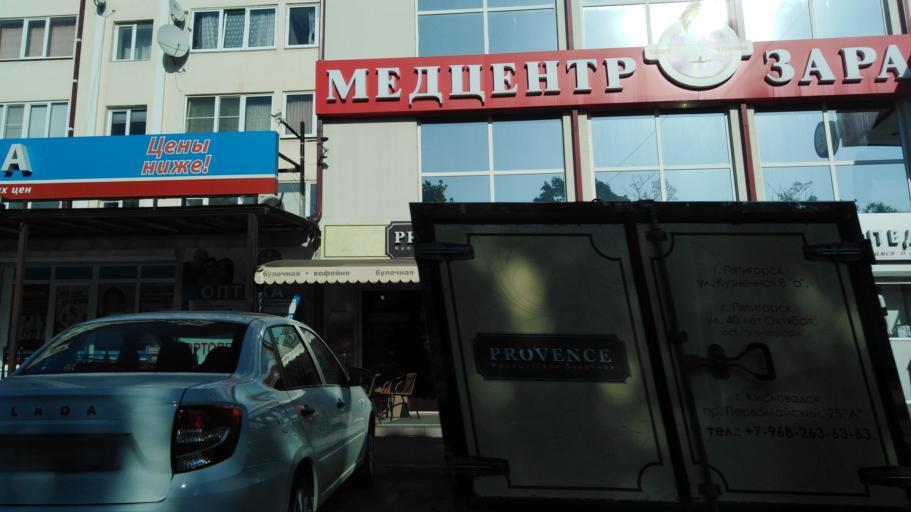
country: RU
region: Stavropol'skiy
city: Pyatigorsk
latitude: 44.0461
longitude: 43.0687
